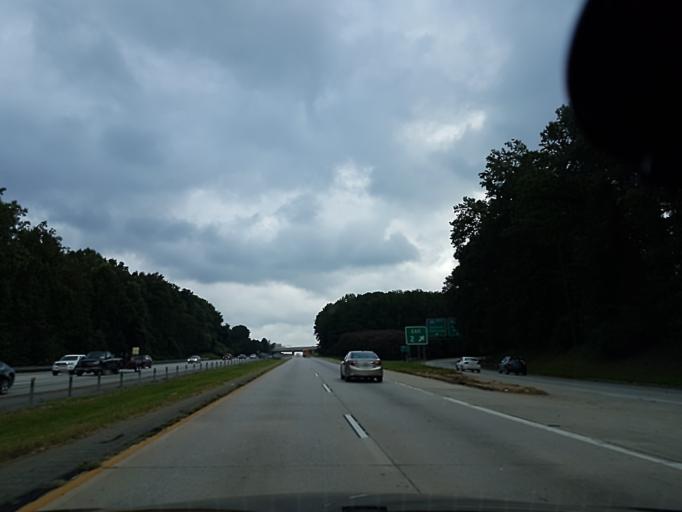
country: US
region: Georgia
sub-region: DeKalb County
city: Clarkston
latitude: 33.8128
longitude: -84.2576
